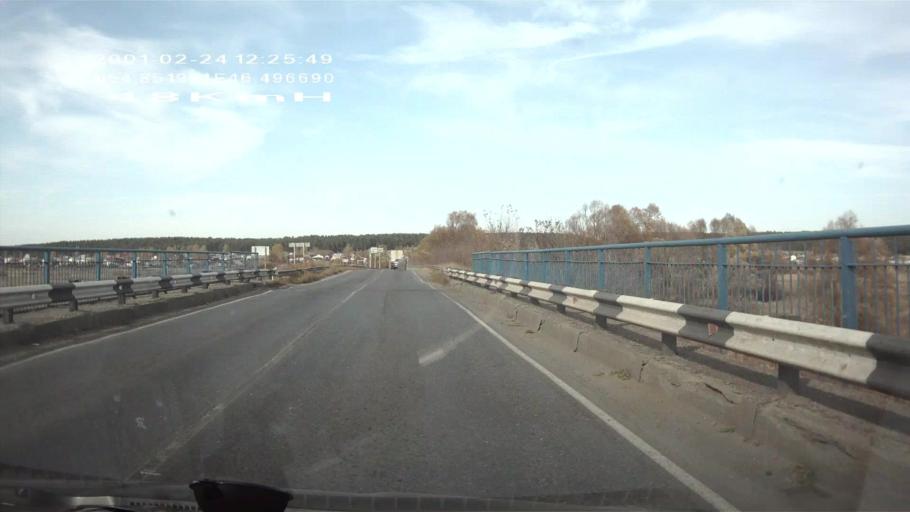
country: RU
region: Chuvashia
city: Alatyr'
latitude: 54.8521
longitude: 46.4966
